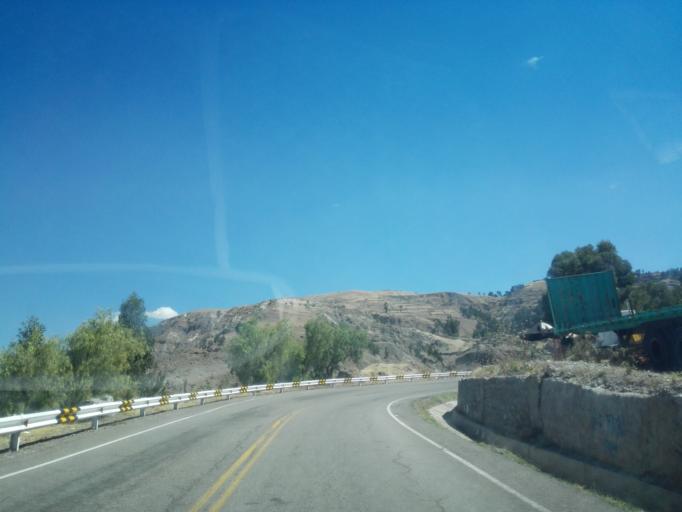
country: PE
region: Ayacucho
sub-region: Provincia de Huamanga
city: Ayacucho
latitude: -13.1685
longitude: -74.2418
